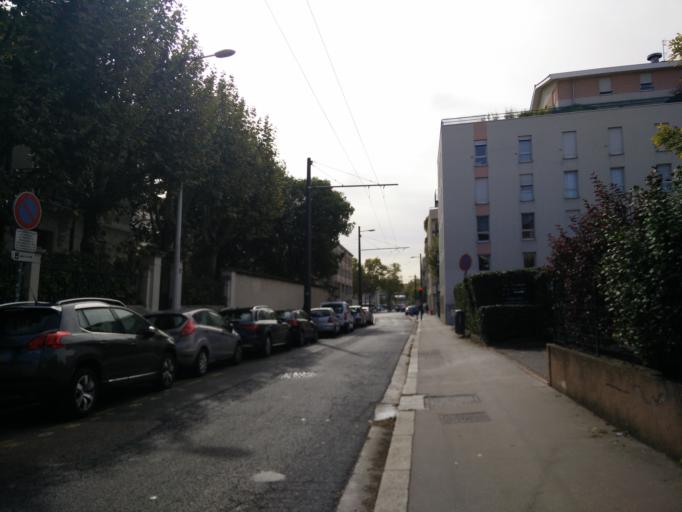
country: FR
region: Rhone-Alpes
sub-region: Departement du Rhone
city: Villeurbanne
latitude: 45.7454
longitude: 4.8795
